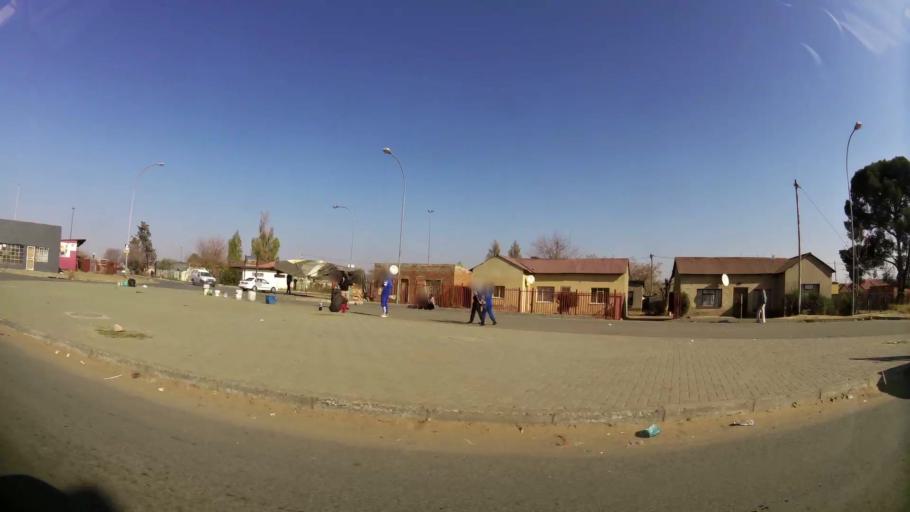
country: ZA
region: Orange Free State
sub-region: Mangaung Metropolitan Municipality
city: Bloemfontein
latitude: -29.1406
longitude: 26.2374
